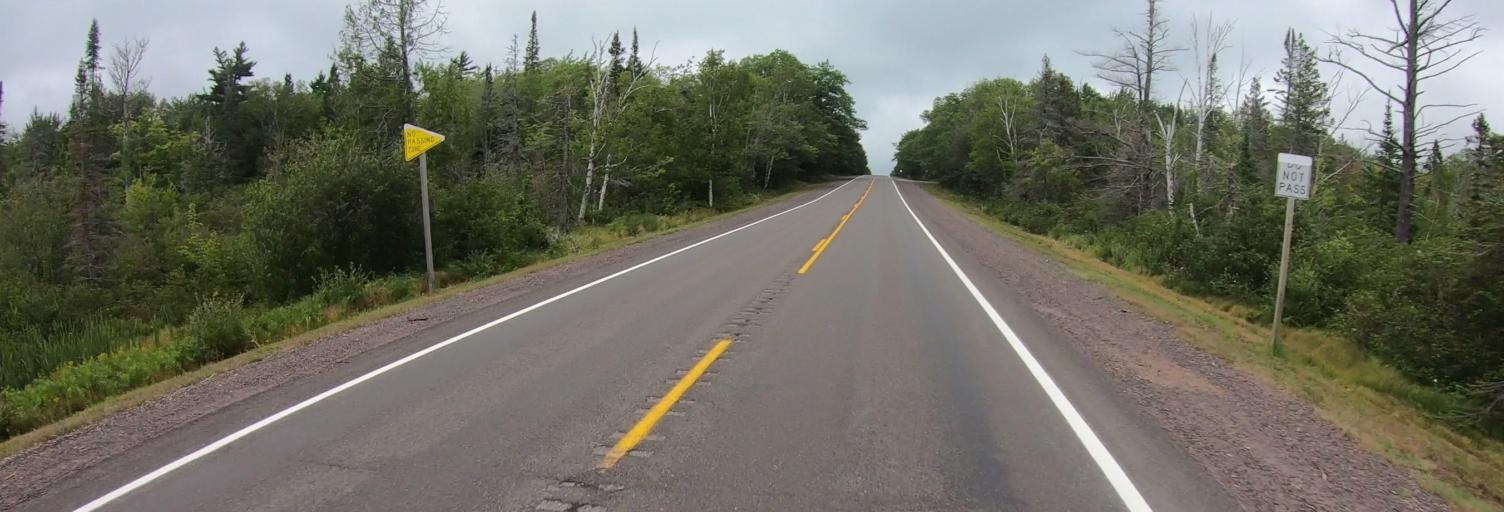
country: US
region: Michigan
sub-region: Keweenaw County
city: Eagle River
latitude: 47.3455
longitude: -88.3135
